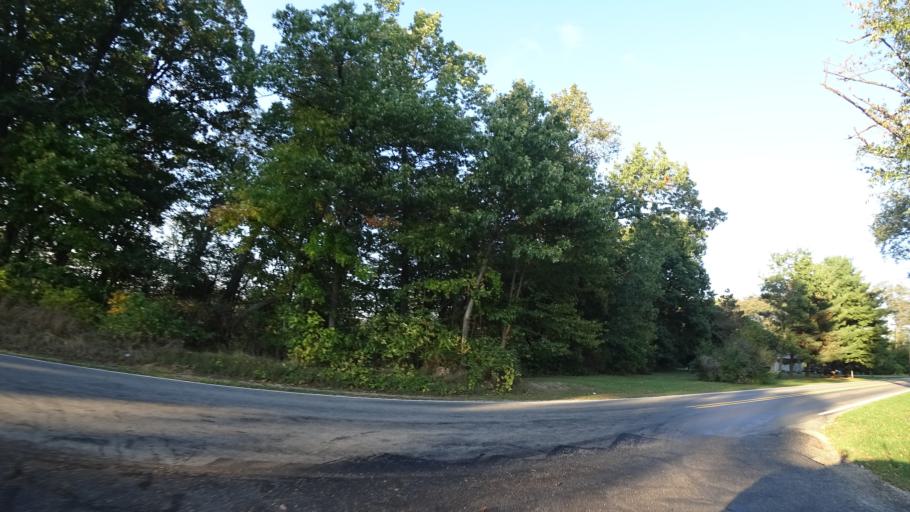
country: US
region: Michigan
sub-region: Saint Joseph County
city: Three Rivers
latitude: 41.9489
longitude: -85.6561
